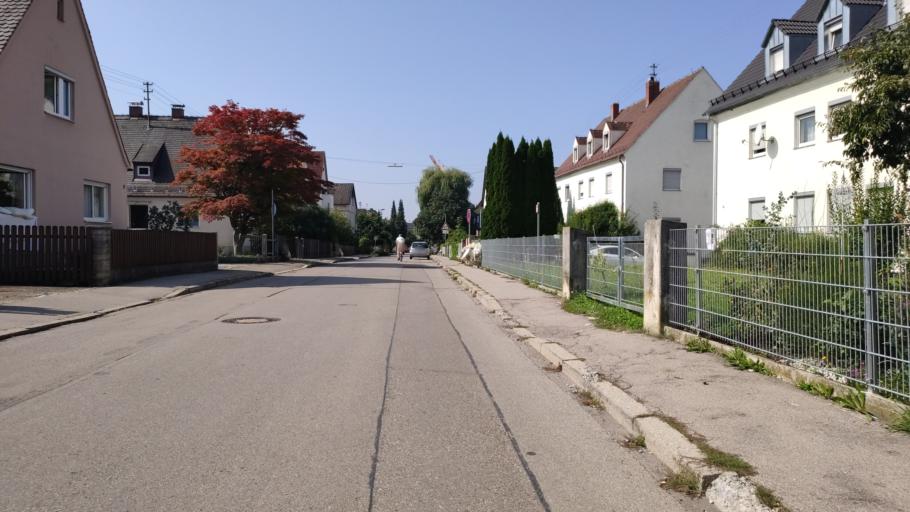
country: DE
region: Bavaria
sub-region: Swabia
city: Bobingen
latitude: 48.2647
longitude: 10.8334
